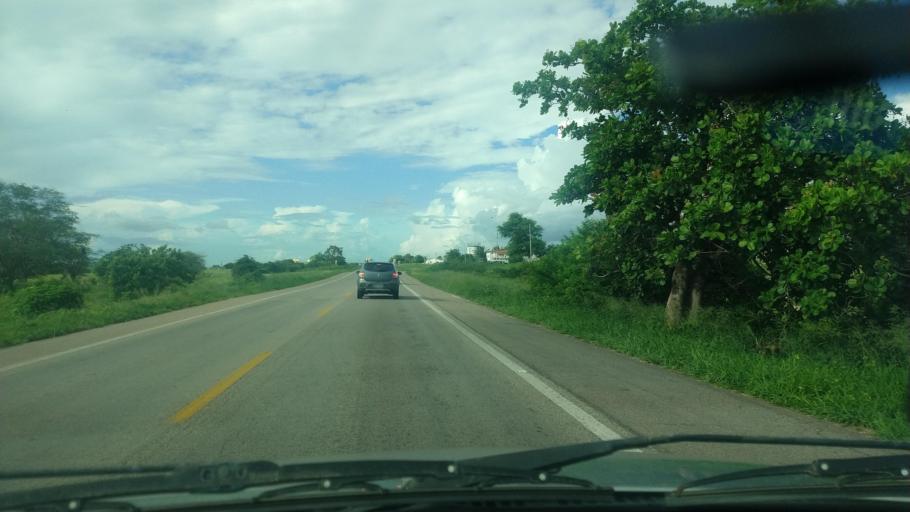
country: BR
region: Rio Grande do Norte
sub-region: Tangara
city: Tangara
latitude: -6.1774
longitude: -35.7687
